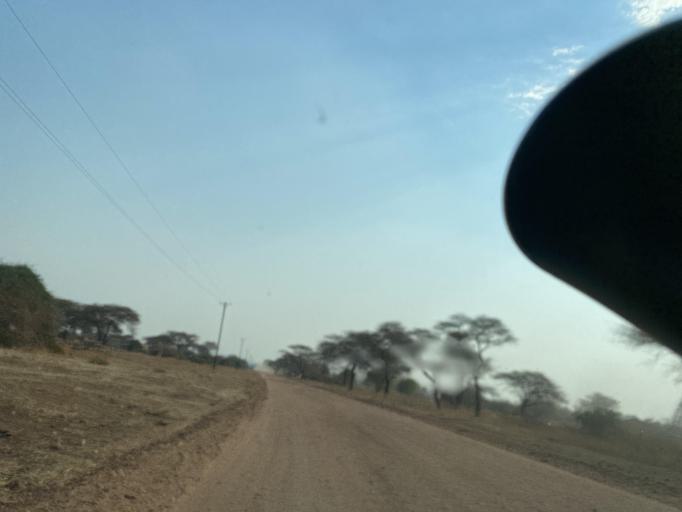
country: ZW
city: Chirundu
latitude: -15.9203
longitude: 28.9755
